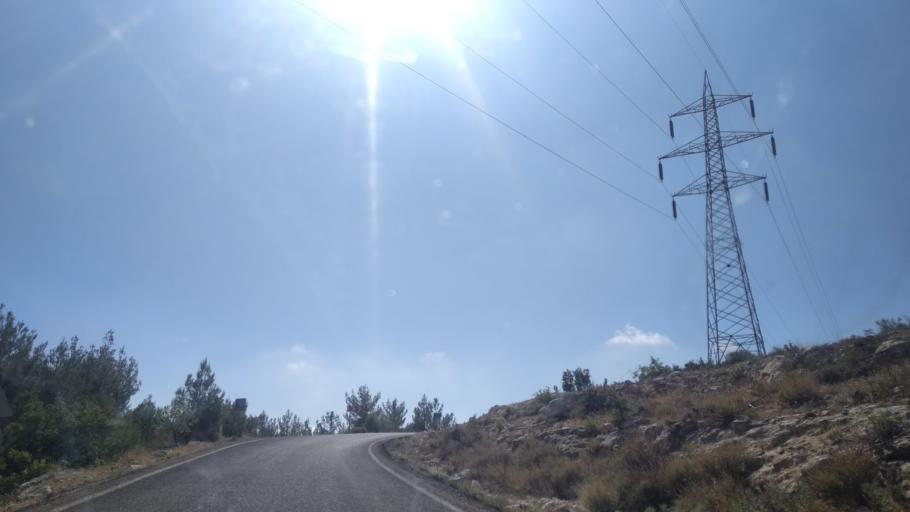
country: TR
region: Mersin
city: Gulnar
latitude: 36.3055
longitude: 33.4493
